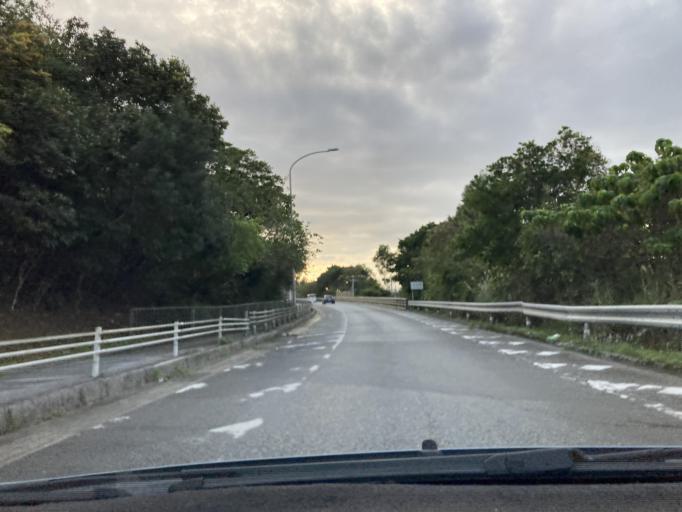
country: JP
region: Okinawa
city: Ishikawa
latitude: 26.4385
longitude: 127.8060
